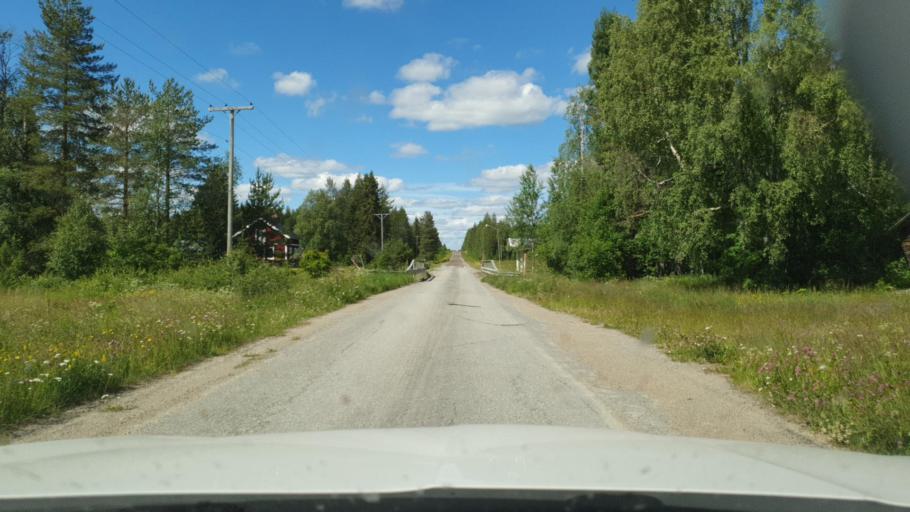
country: SE
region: Vaesterbotten
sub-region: Skelleftea Kommun
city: Backa
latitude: 65.1668
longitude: 21.1268
